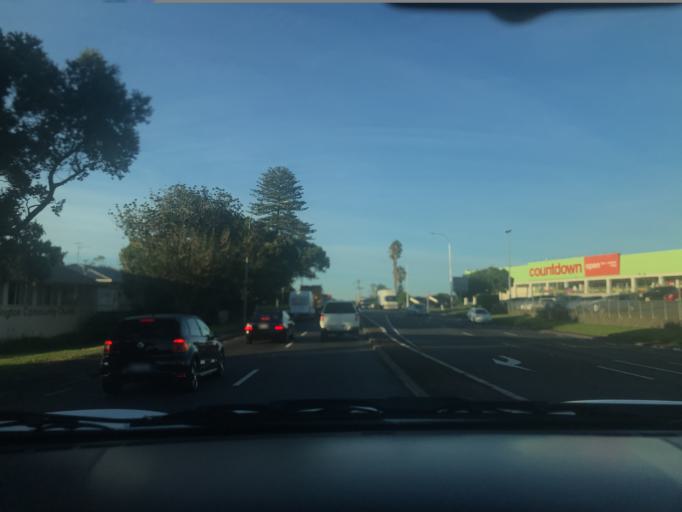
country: NZ
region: Auckland
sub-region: Auckland
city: Tamaki
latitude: -36.9089
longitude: 174.8386
